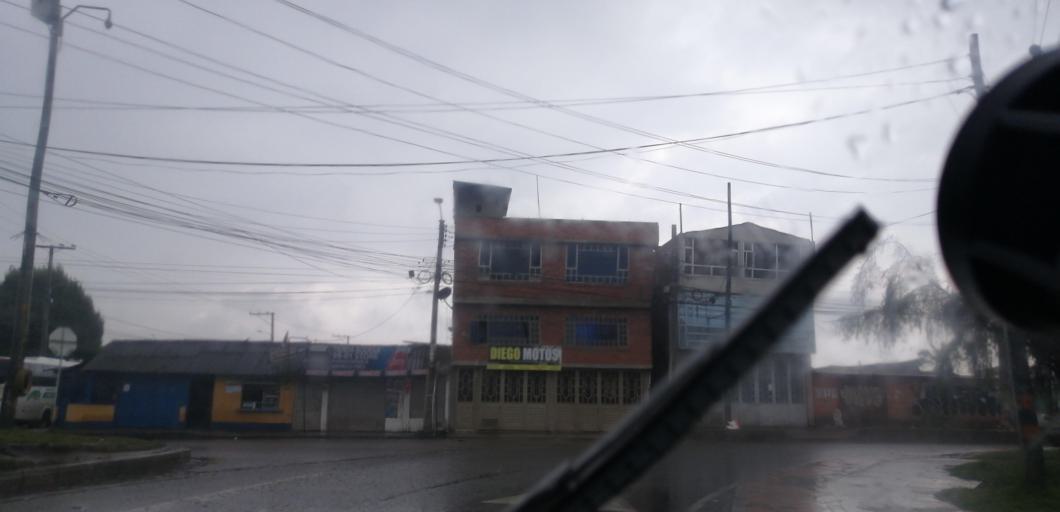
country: CO
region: Cundinamarca
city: Madrid
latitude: 4.7394
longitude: -74.2546
